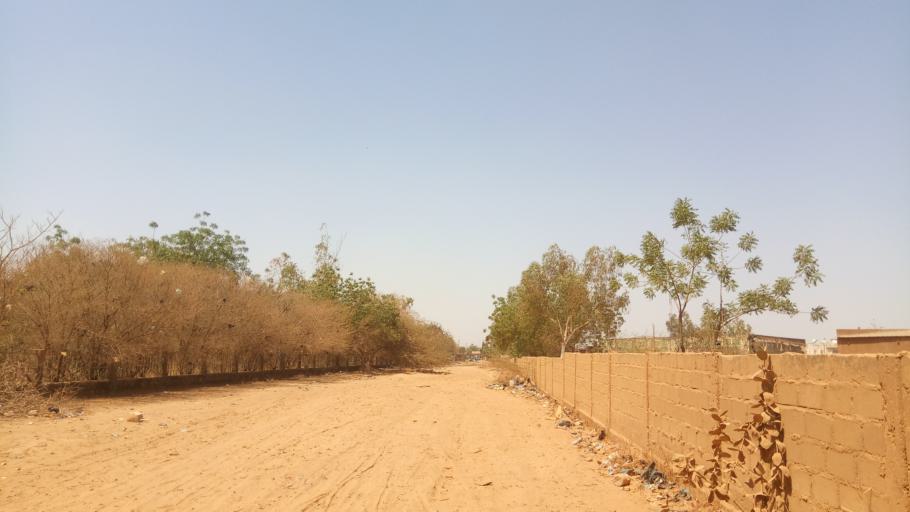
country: BF
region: Centre
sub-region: Kadiogo Province
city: Ouagadougou
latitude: 12.3938
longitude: -1.5693
